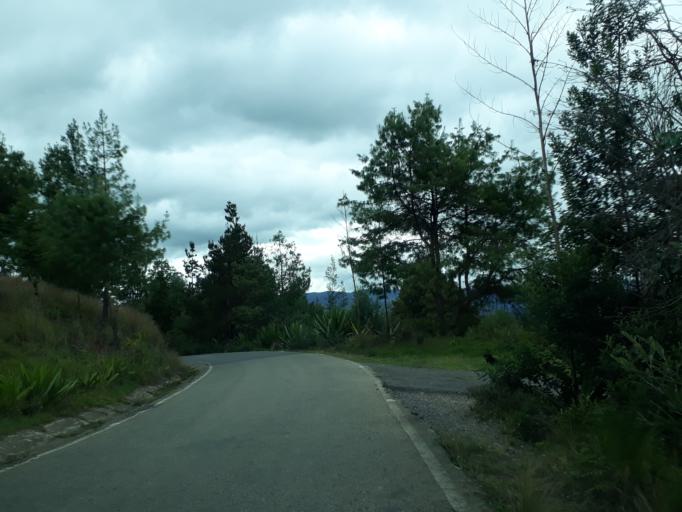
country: CO
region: Cundinamarca
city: Susa
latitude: 5.4008
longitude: -73.7738
